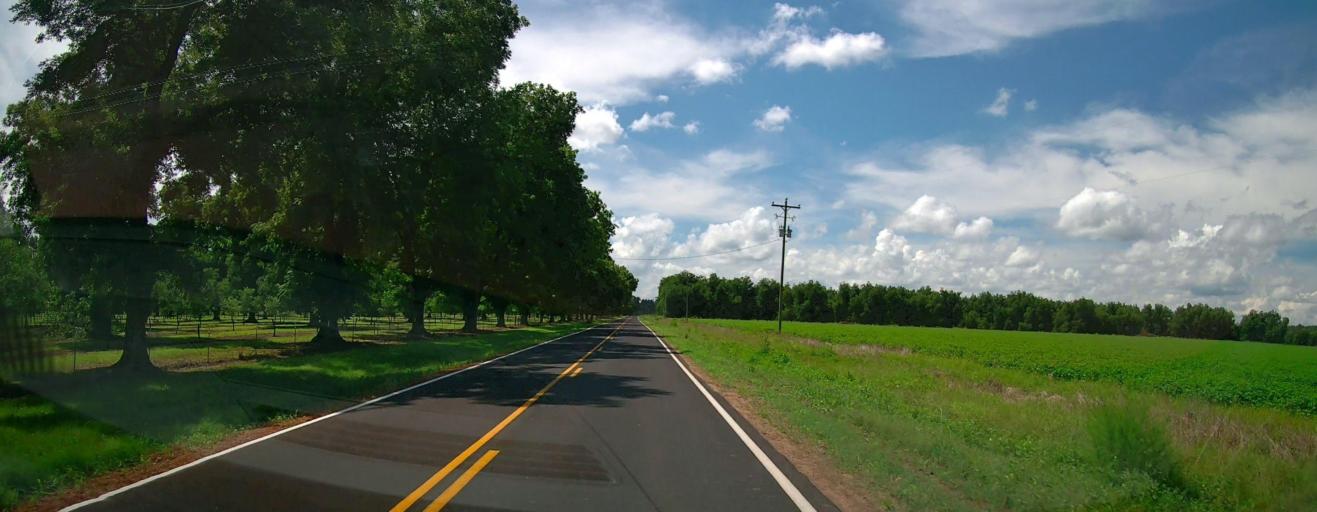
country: US
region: Georgia
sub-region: Macon County
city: Marshallville
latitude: 32.4727
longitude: -83.8800
